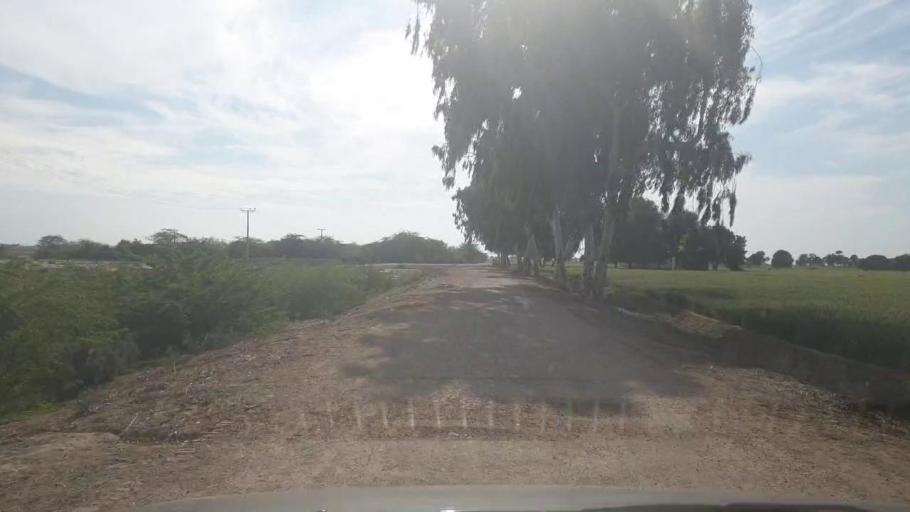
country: PK
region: Sindh
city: Pithoro
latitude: 25.4037
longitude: 69.2476
